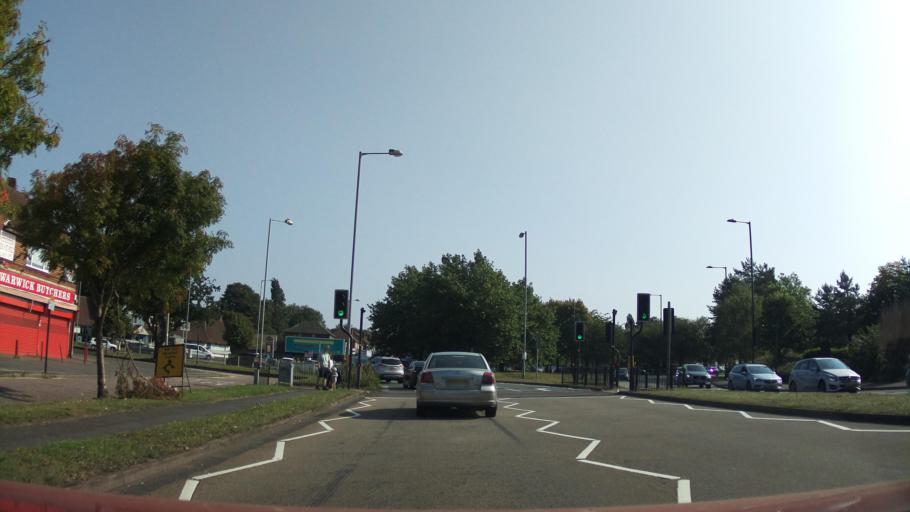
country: GB
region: England
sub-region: Walsall
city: Streetly
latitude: 52.5526
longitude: -1.9101
